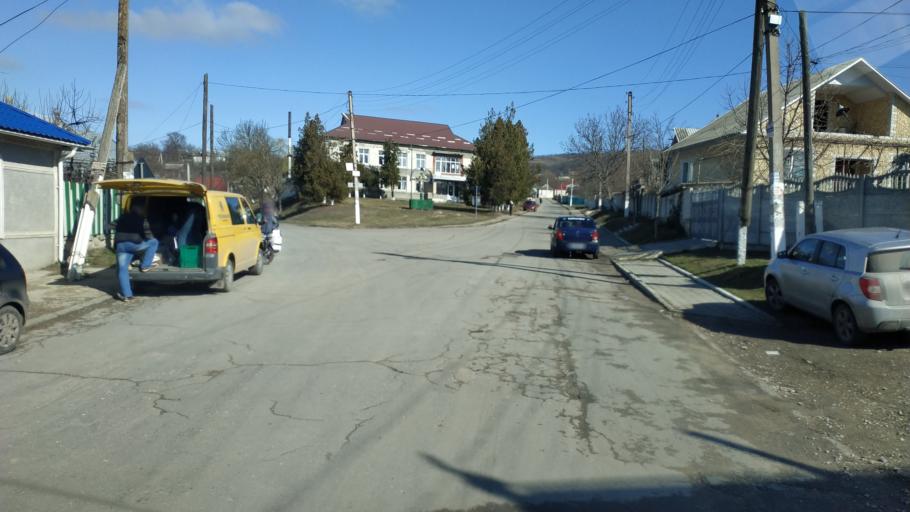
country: MD
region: Straseni
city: Straseni
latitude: 47.0155
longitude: 28.5432
